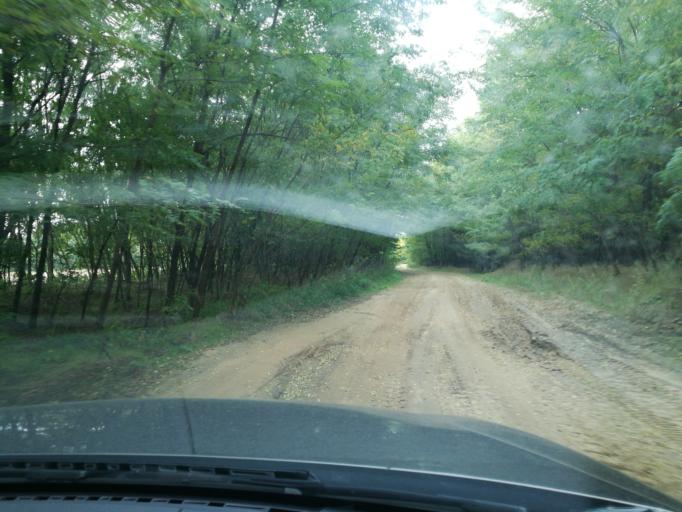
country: HU
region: Szabolcs-Szatmar-Bereg
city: Apagy
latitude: 47.9982
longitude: 21.9131
